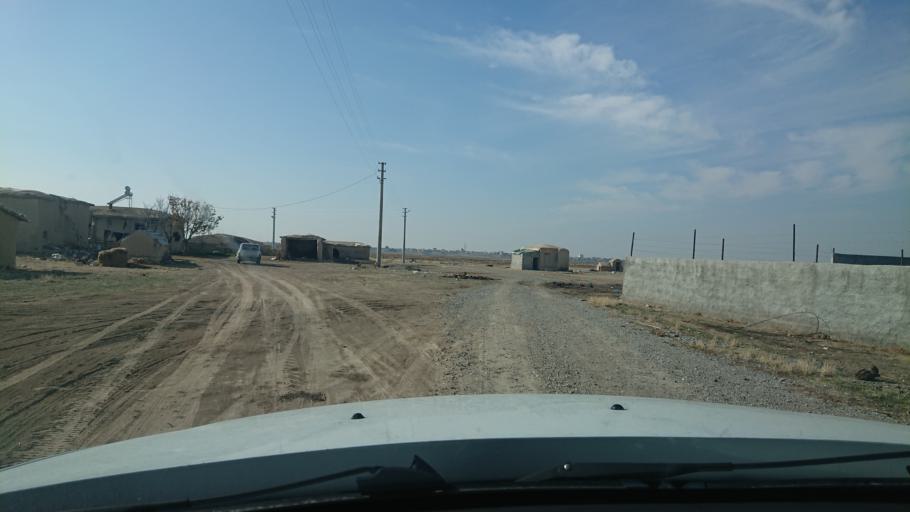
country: TR
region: Aksaray
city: Sultanhani
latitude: 38.2608
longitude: 33.4731
